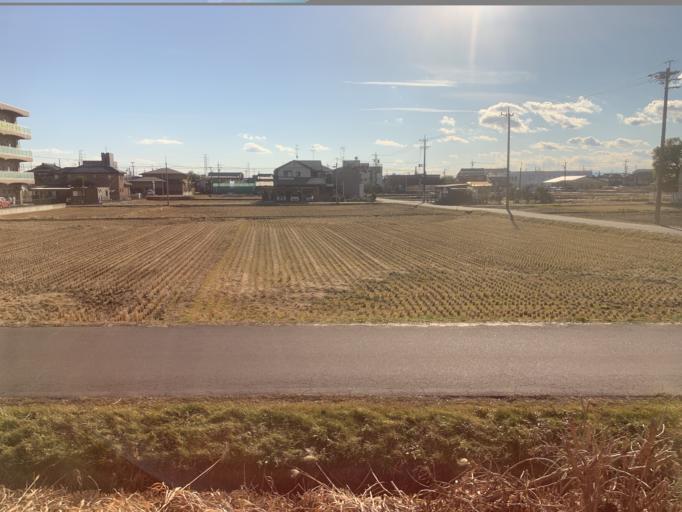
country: JP
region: Gifu
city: Gifu-shi
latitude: 35.4043
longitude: 136.7899
